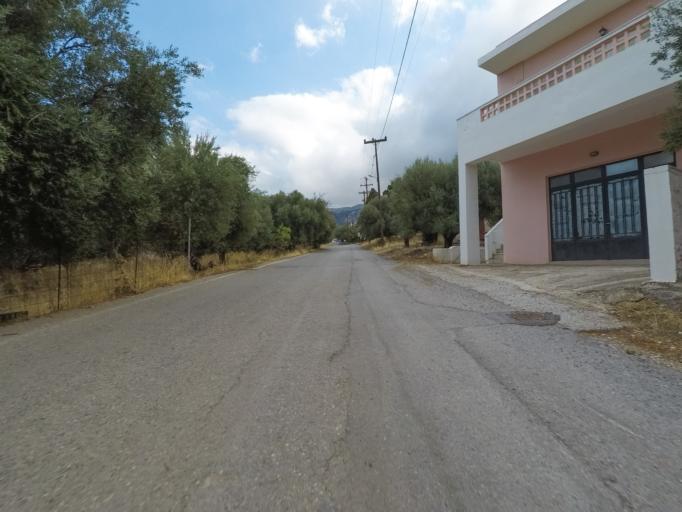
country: GR
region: Crete
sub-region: Nomos Lasithiou
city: Kritsa
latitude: 35.1577
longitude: 25.6484
